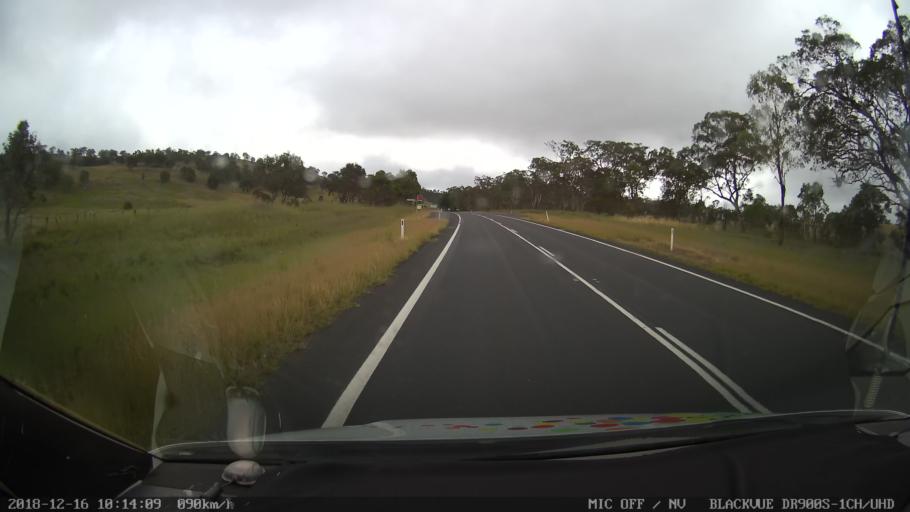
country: AU
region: New South Wales
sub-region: Tenterfield Municipality
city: Carrolls Creek
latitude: -29.2902
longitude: 151.9606
